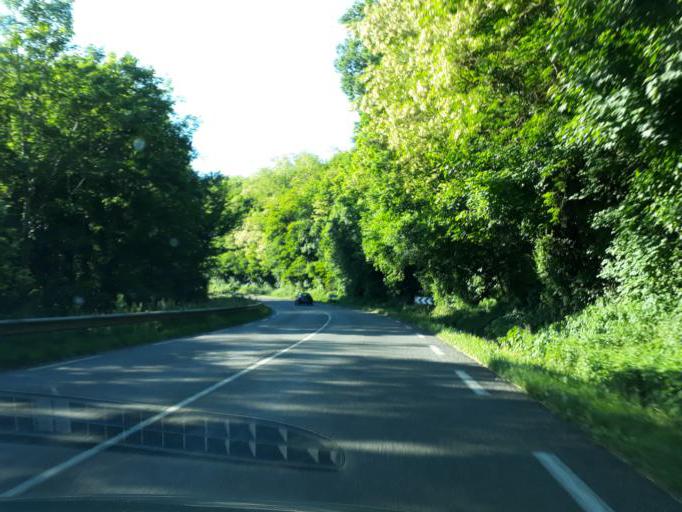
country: FR
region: Bourgogne
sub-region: Departement de la Nievre
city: Neuvy-sur-Loire
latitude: 47.4910
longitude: 2.9195
